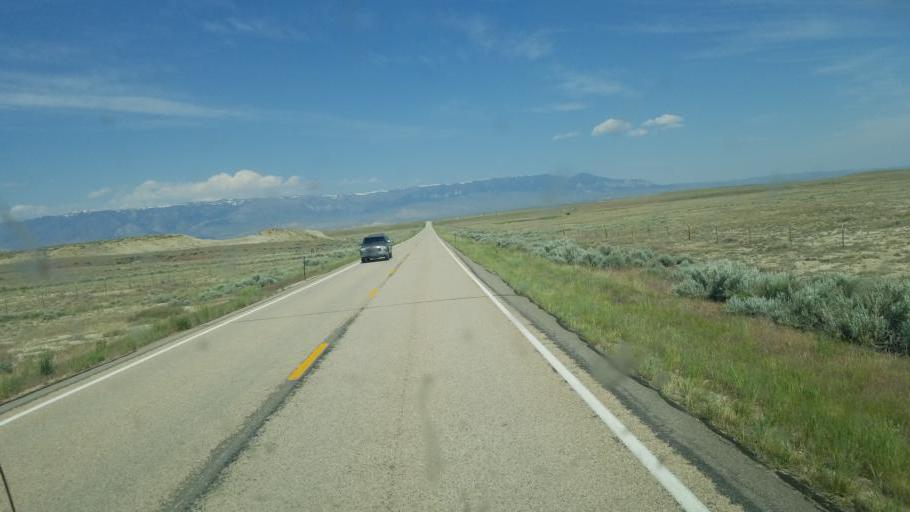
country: US
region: Wyoming
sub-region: Park County
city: Powell
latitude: 44.8496
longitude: -109.0081
